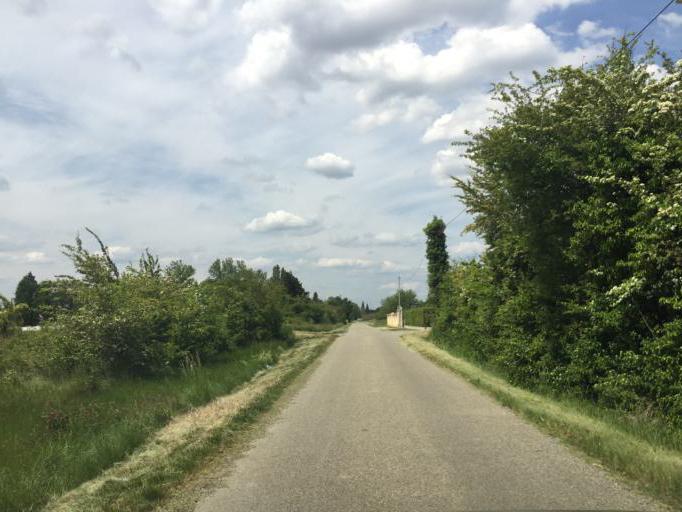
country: FR
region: Provence-Alpes-Cote d'Azur
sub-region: Departement du Vaucluse
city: Jonquieres
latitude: 44.1212
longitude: 4.8867
